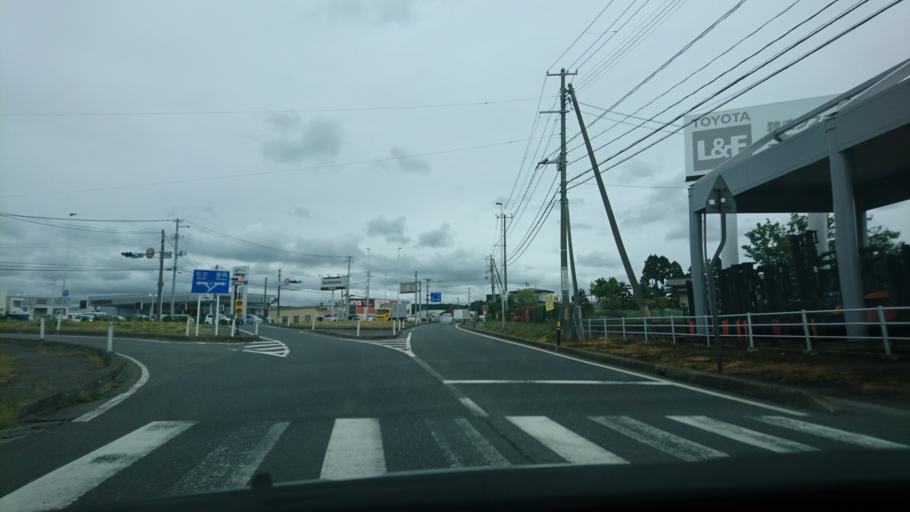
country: JP
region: Iwate
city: Ichinoseki
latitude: 38.9692
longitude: 141.1196
